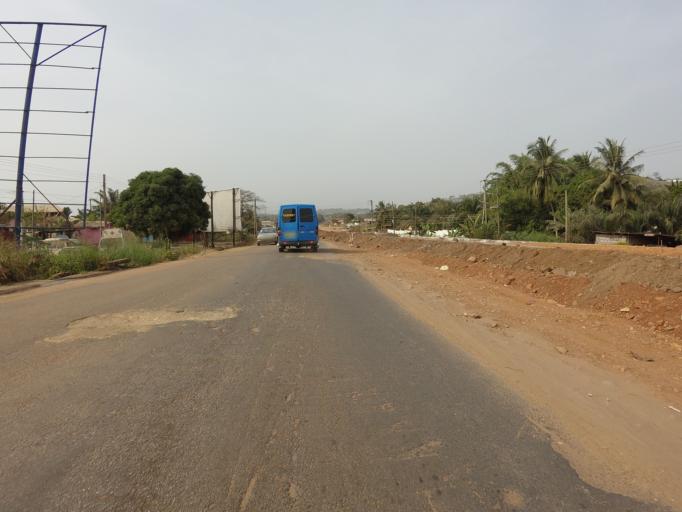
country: GH
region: Volta
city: Ho
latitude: 6.5999
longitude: 0.4491
